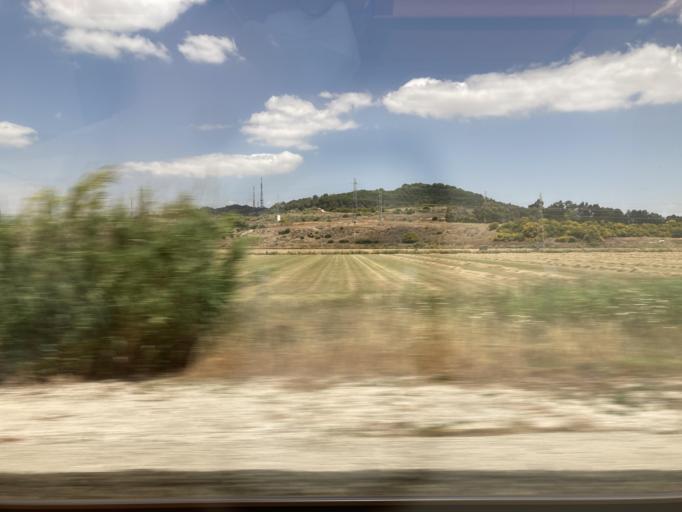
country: ES
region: Andalusia
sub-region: Provincia de Cadiz
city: Jerez de la Frontera
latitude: 36.6210
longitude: -6.1492
